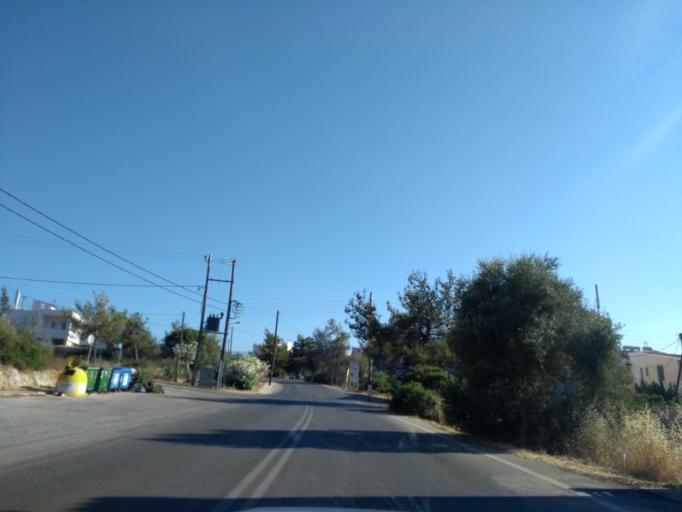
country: GR
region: Crete
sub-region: Nomos Chanias
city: Pithari
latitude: 35.5475
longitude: 24.0829
